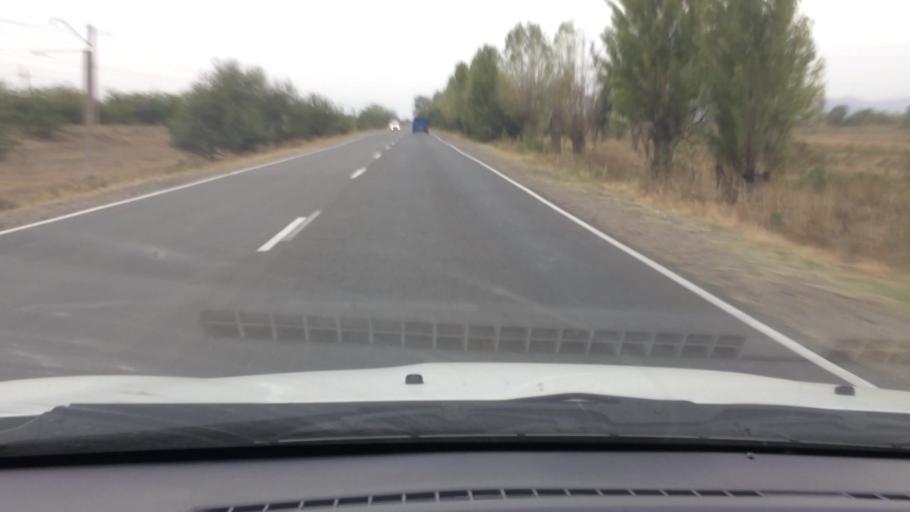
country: GE
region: Kvemo Kartli
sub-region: Marneuli
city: Marneuli
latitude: 41.4488
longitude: 44.8144
